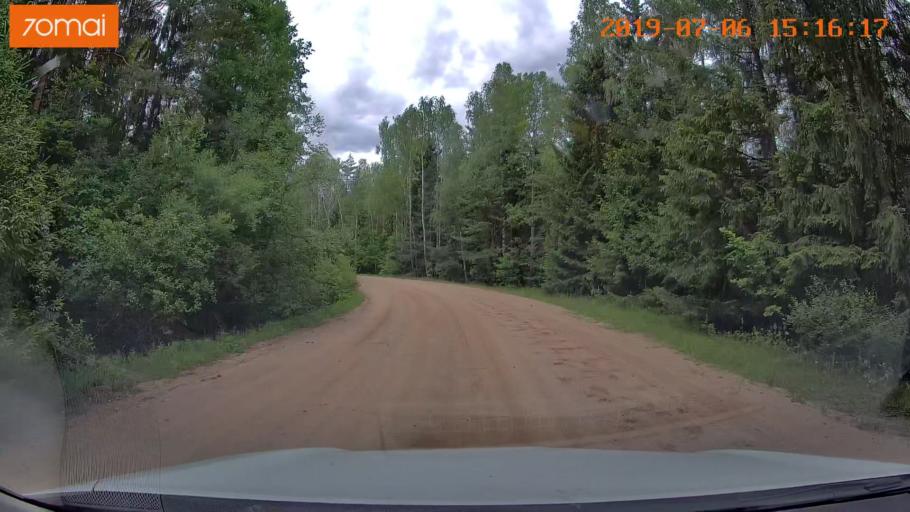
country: BY
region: Minsk
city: Ivyanyets
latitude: 53.9800
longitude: 26.6801
